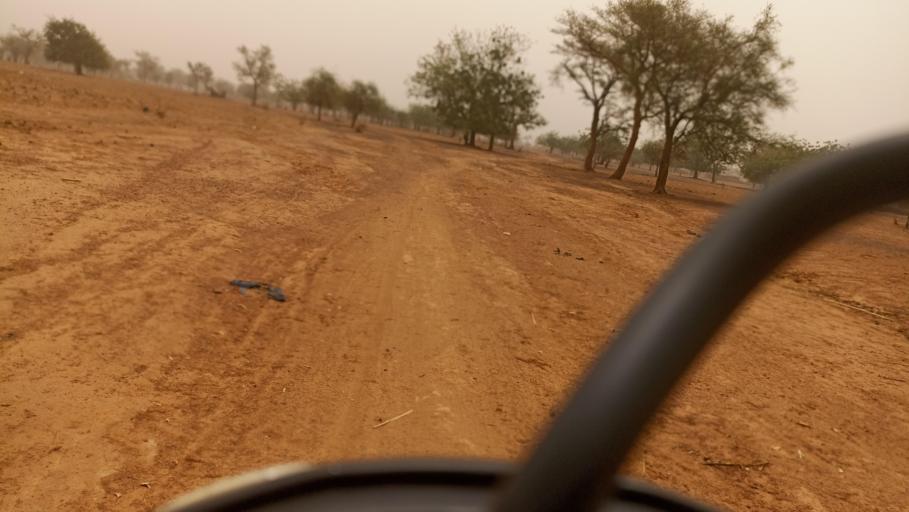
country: BF
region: Nord
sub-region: Province du Zondoma
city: Gourcy
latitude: 13.2486
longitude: -2.5959
